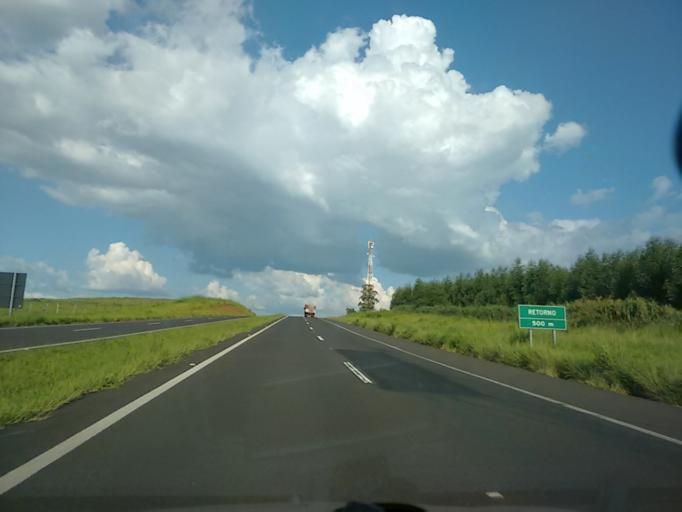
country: BR
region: Sao Paulo
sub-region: Duartina
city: Duartina
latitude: -22.3248
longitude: -49.4226
